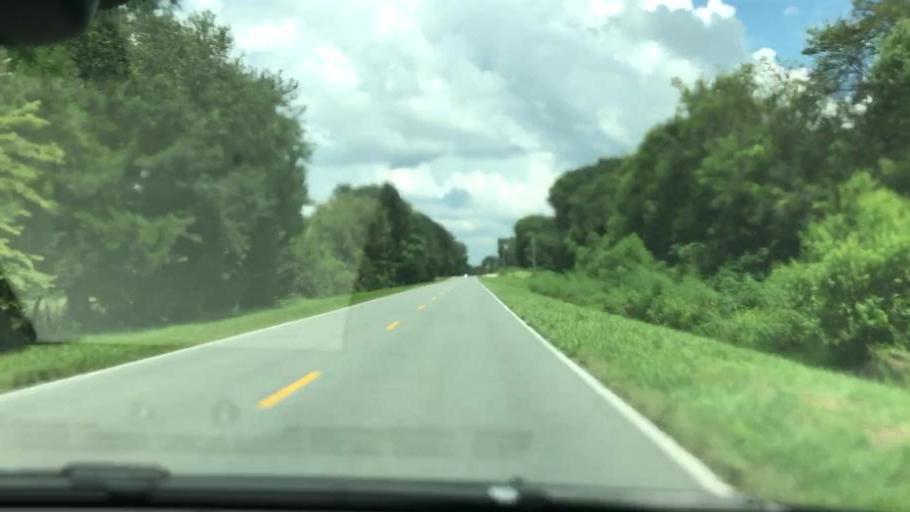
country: US
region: Florida
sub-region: Jackson County
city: Malone
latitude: 30.9007
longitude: -85.1342
